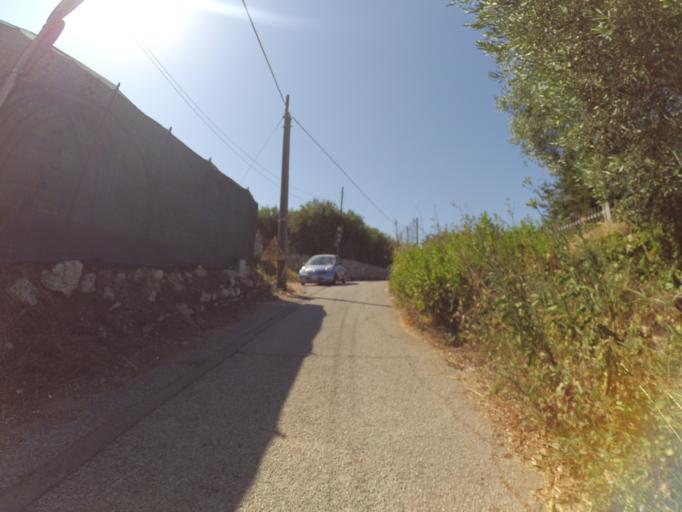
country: IT
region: Latium
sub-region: Provincia di Latina
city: Gaeta
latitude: 41.2204
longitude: 13.5485
